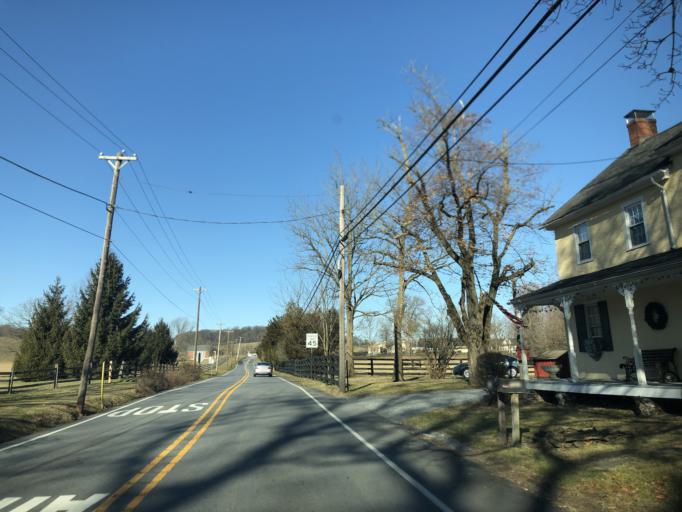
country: US
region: Pennsylvania
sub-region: Chester County
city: Upland
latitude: 39.9167
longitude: -75.8182
